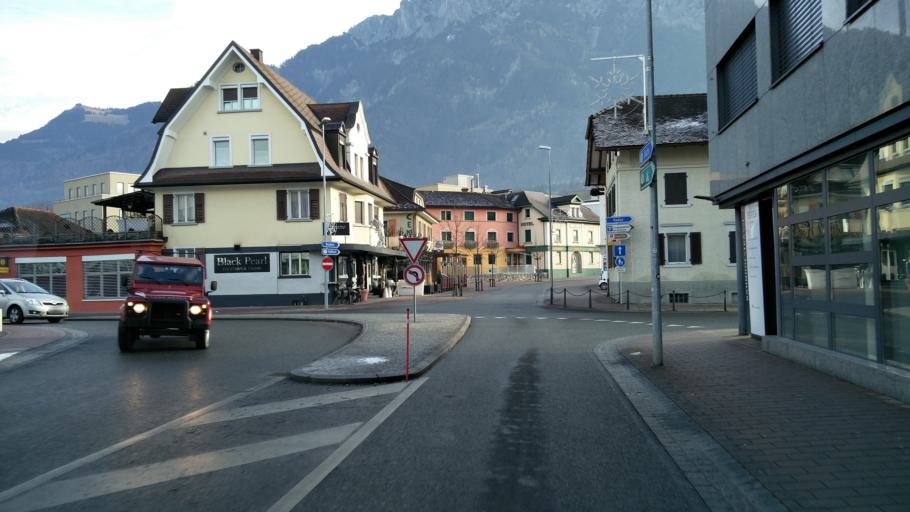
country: LI
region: Schaan
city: Schaan
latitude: 47.1674
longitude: 9.5085
